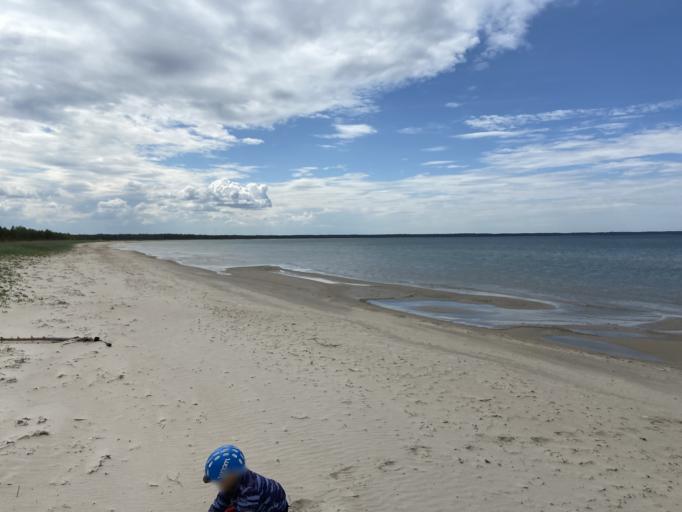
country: EE
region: Harju
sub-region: Paldiski linn
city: Paldiski
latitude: 59.2487
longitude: 23.7440
